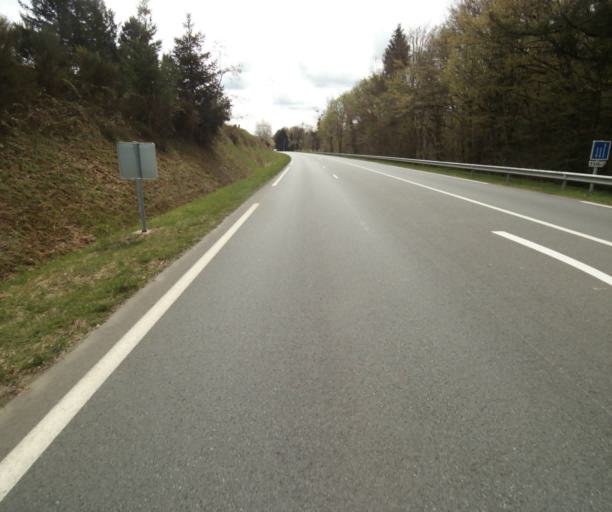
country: FR
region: Limousin
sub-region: Departement de la Correze
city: Sainte-Fortunade
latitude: 45.2082
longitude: 1.8262
